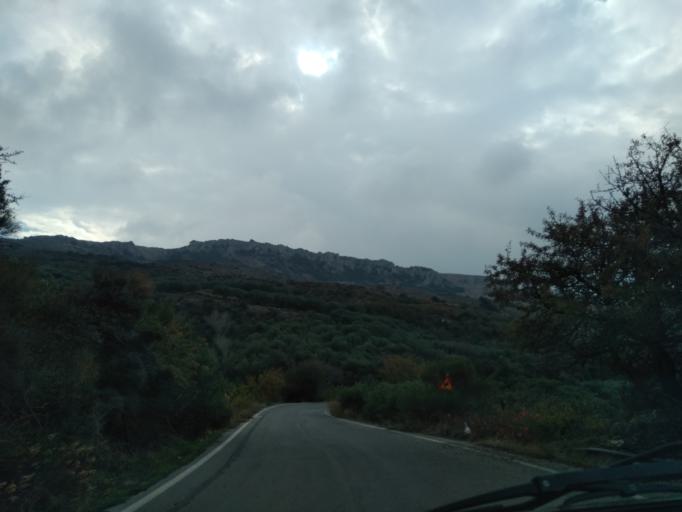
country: GR
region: Crete
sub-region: Nomos Lasithiou
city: Siteia
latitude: 35.1373
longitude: 26.0216
